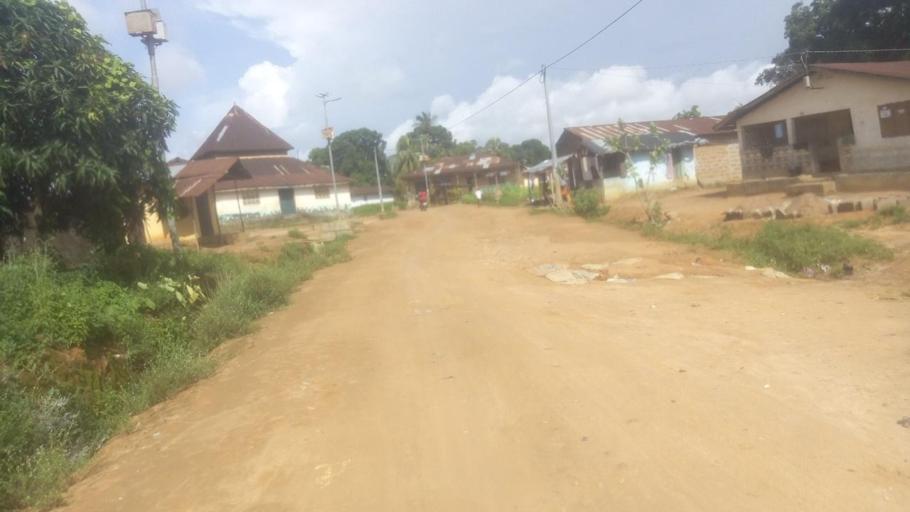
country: SL
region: Northern Province
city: Masoyila
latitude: 8.6111
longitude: -13.1921
